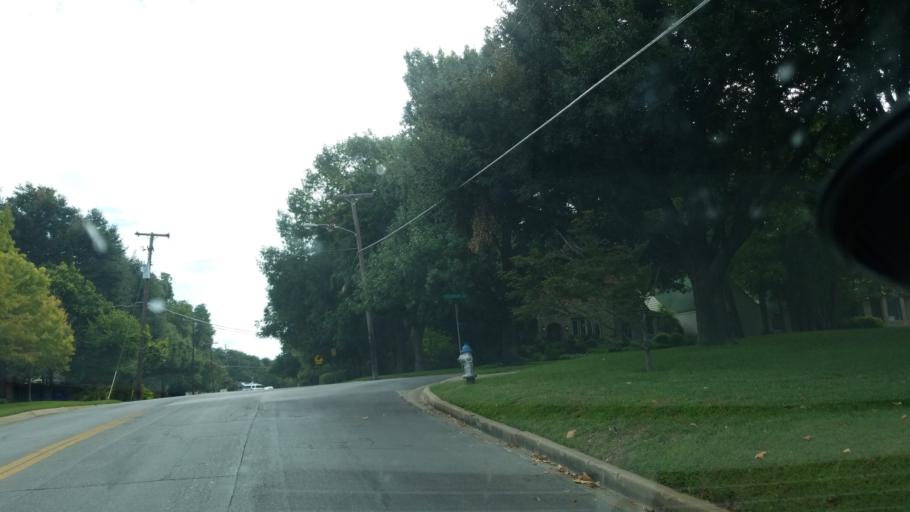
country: US
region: Texas
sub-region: Dallas County
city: Dallas
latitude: 32.7594
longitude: -96.8418
